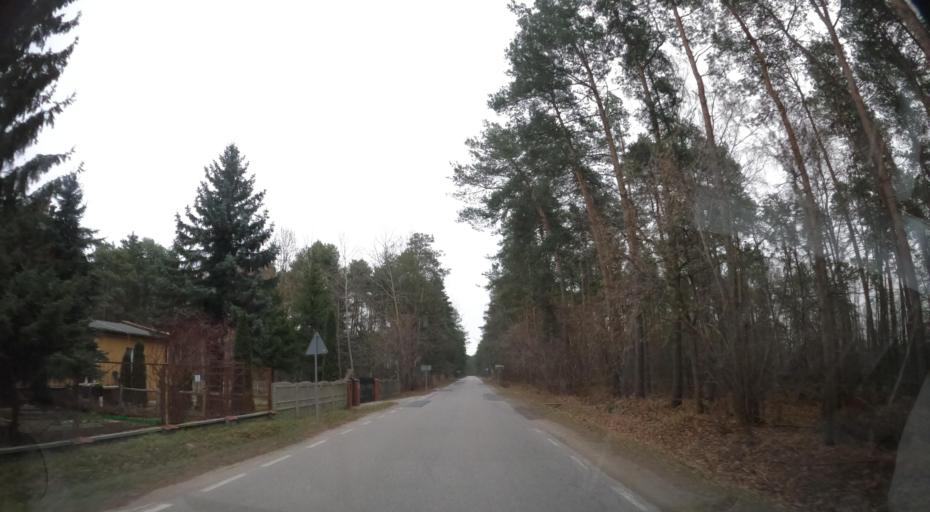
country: PL
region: Masovian Voivodeship
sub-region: Powiat radomski
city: Jedlinsk
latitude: 51.4934
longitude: 21.1462
